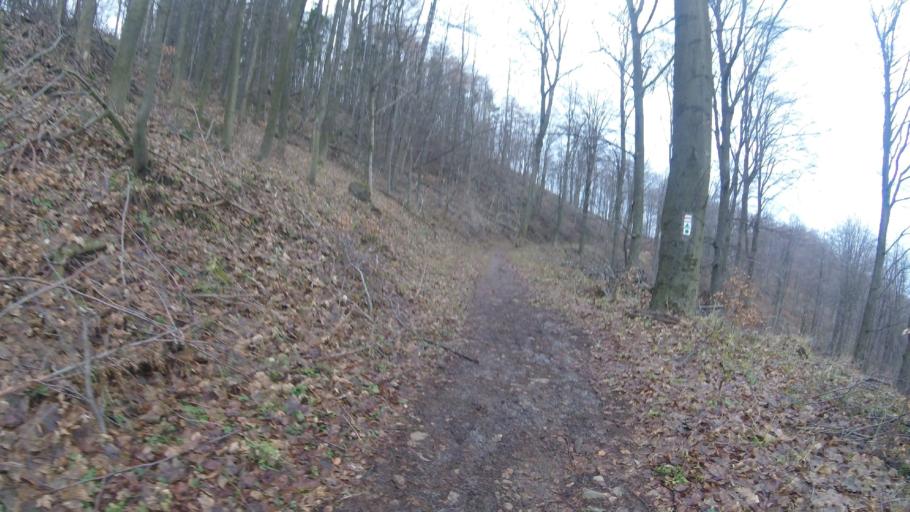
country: HU
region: Heves
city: Paradsasvar
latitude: 47.9188
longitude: 19.9249
